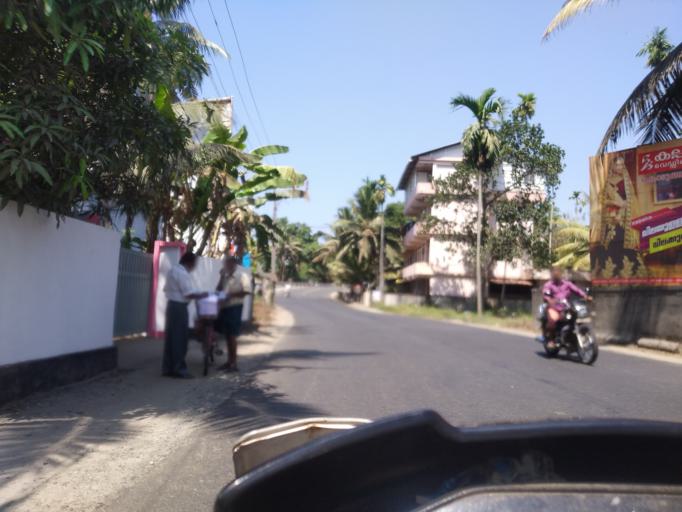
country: IN
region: Kerala
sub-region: Thrissur District
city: Kodungallur
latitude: 10.1695
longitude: 76.2126
